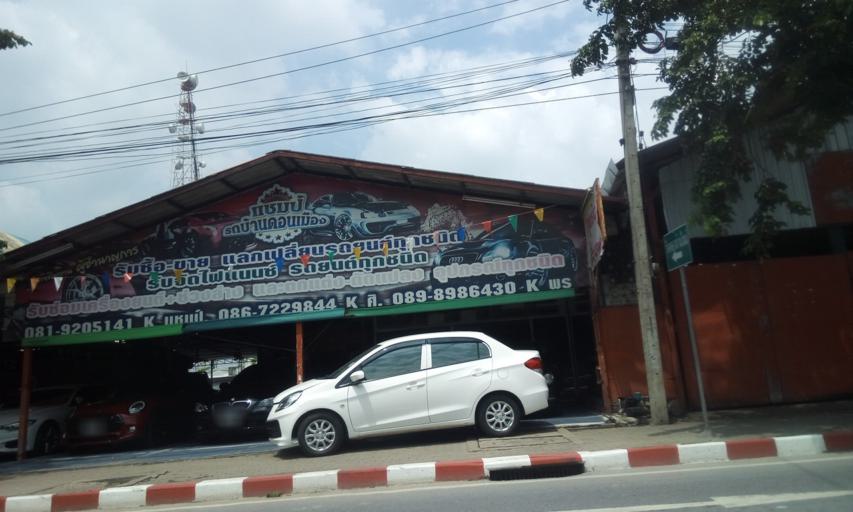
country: TH
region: Bangkok
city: Don Mueang
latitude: 13.9333
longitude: 100.5659
